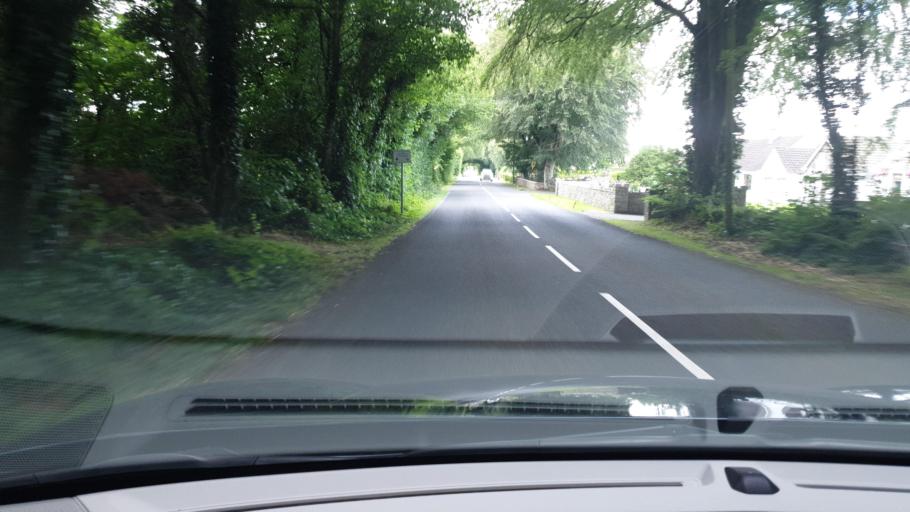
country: IE
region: Leinster
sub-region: An Mhi
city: Dunshaughlin
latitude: 53.5611
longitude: -6.5940
